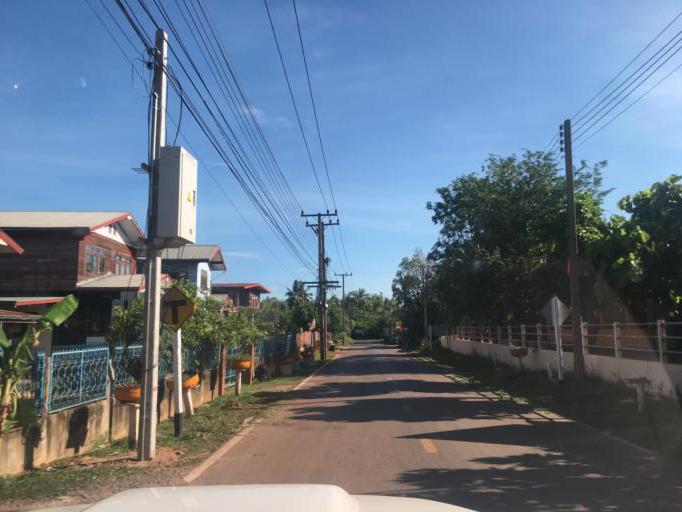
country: TH
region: Changwat Udon Thani
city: Kut Chap
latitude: 17.4949
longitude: 102.5978
